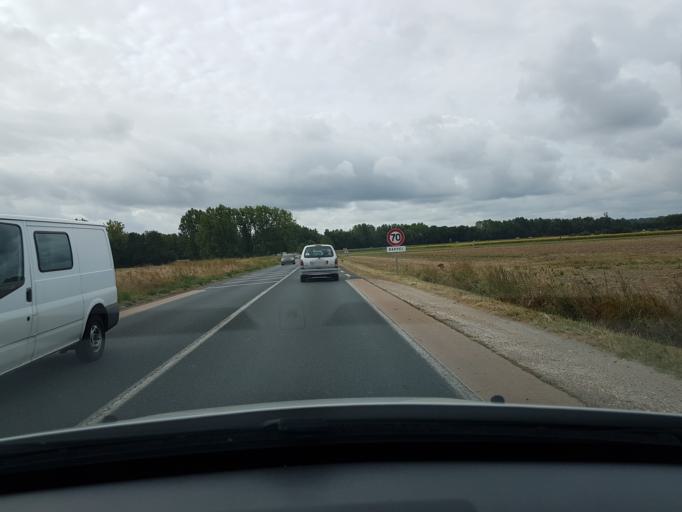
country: FR
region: Centre
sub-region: Departement d'Indre-et-Loire
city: Larcay
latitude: 47.3856
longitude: 0.7853
